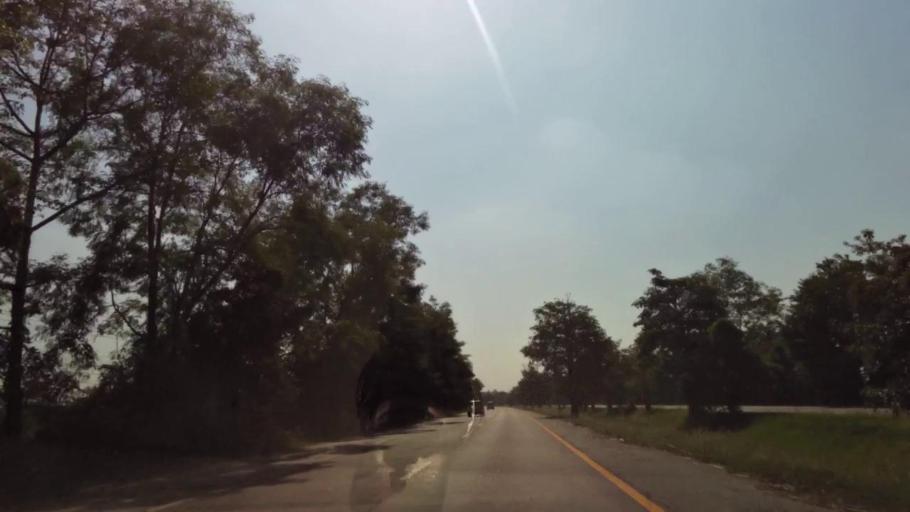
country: TH
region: Phichit
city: Wachira Barami
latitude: 16.6415
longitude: 100.1497
